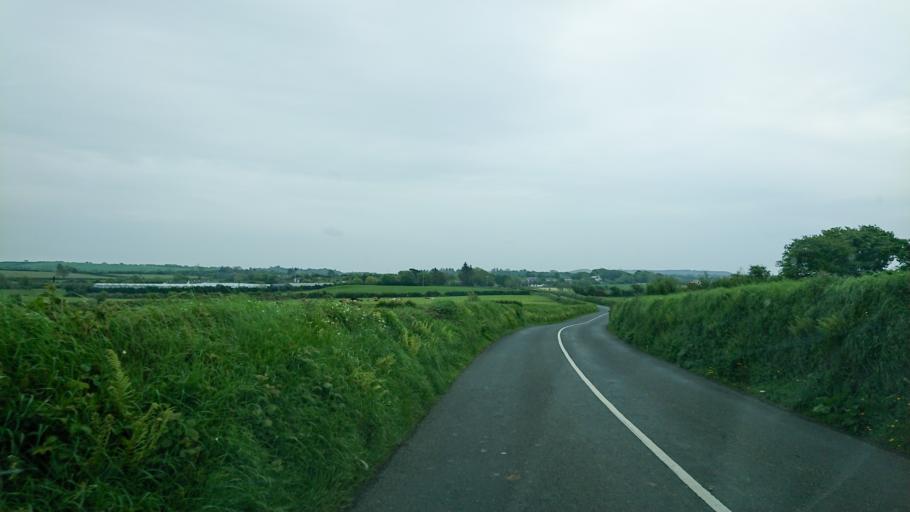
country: IE
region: Munster
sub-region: Waterford
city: Waterford
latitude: 52.2205
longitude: -7.0492
